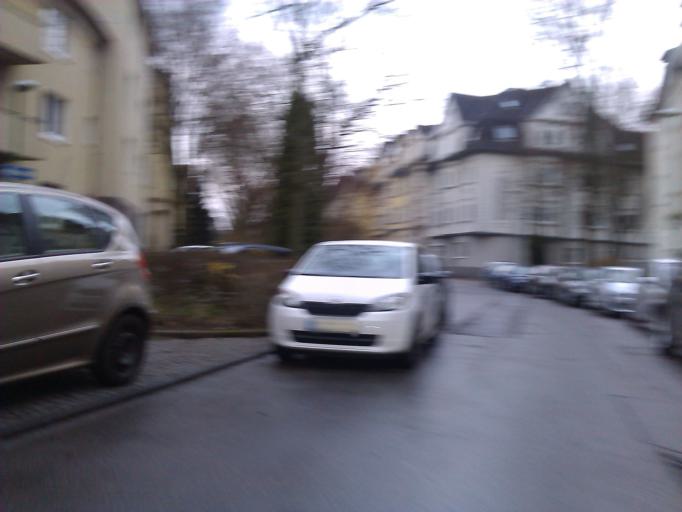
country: DE
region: North Rhine-Westphalia
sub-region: Regierungsbezirk Dusseldorf
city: Essen
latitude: 51.4274
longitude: 6.9979
